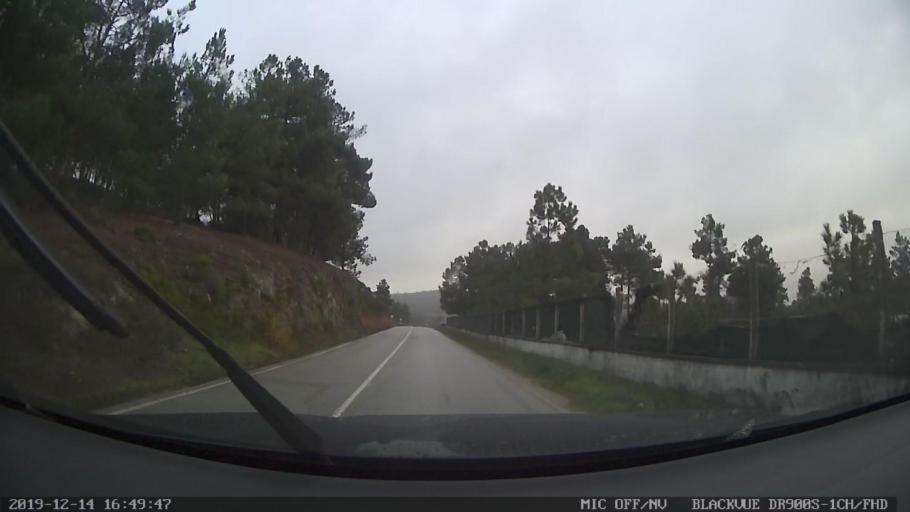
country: PT
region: Vila Real
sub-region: Murca
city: Murca
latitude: 41.4115
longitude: -7.5000
